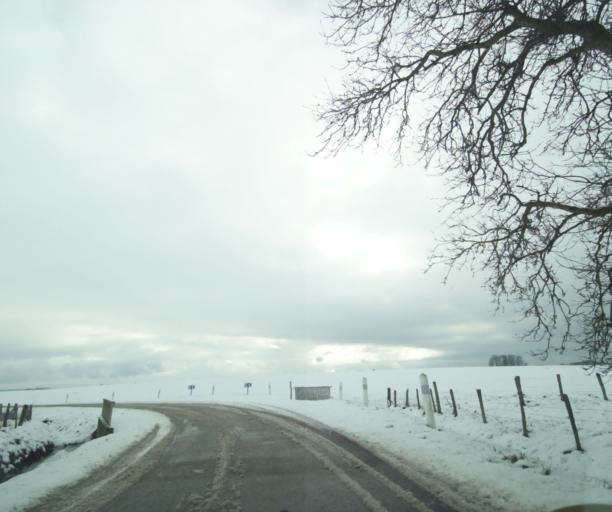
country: FR
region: Champagne-Ardenne
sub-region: Departement de la Haute-Marne
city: Montier-en-Der
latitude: 48.4497
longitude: 4.6963
